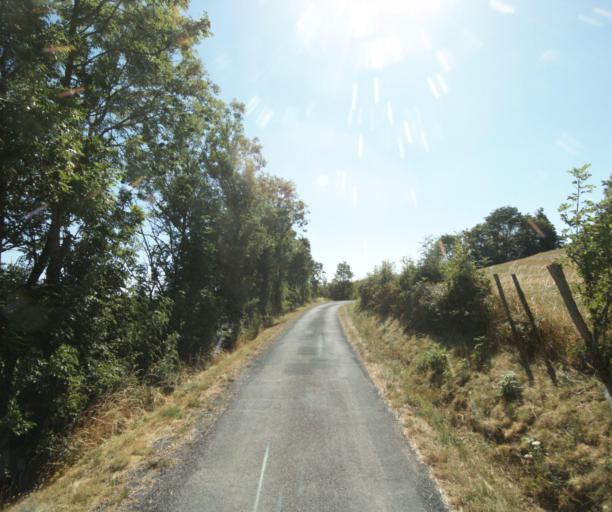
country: FR
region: Rhone-Alpes
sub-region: Departement du Rhone
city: Montrottier
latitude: 45.8145
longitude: 4.4892
